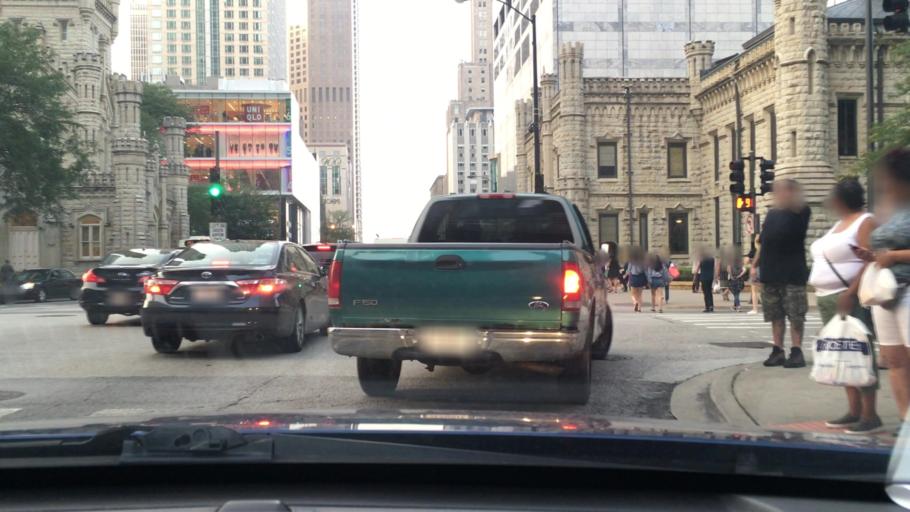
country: US
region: Illinois
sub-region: Cook County
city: Chicago
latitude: 41.8966
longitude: -87.6241
